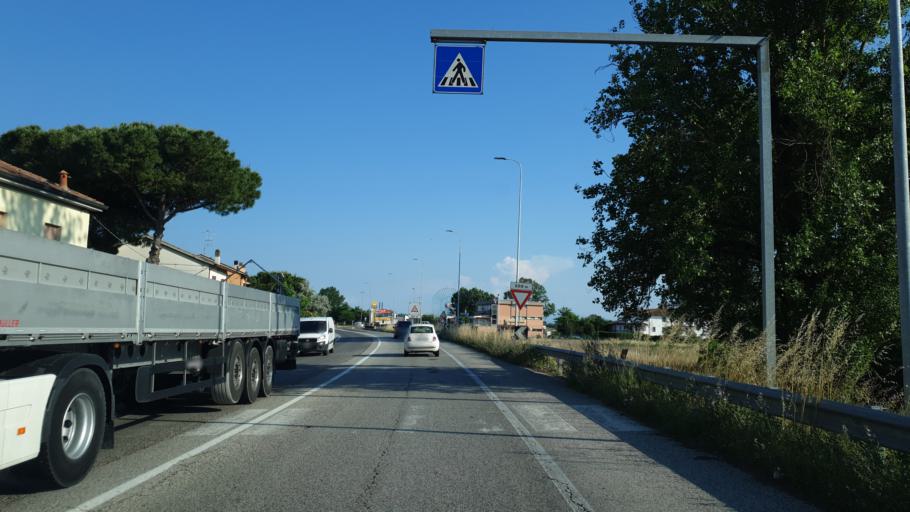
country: IT
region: Emilia-Romagna
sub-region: Provincia di Ravenna
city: Fosso Ghiaia
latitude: 44.3536
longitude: 12.2570
